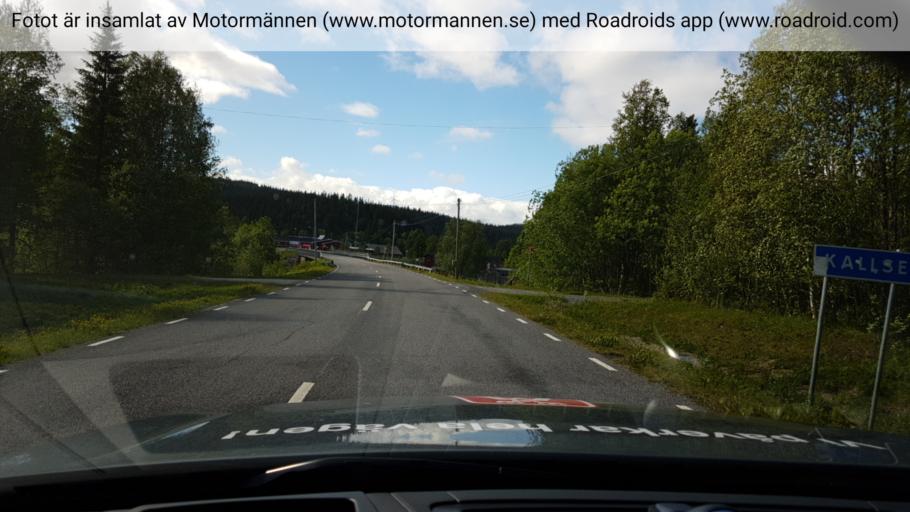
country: SE
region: Jaemtland
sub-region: Are Kommun
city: Are
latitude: 63.7001
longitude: 12.9620
